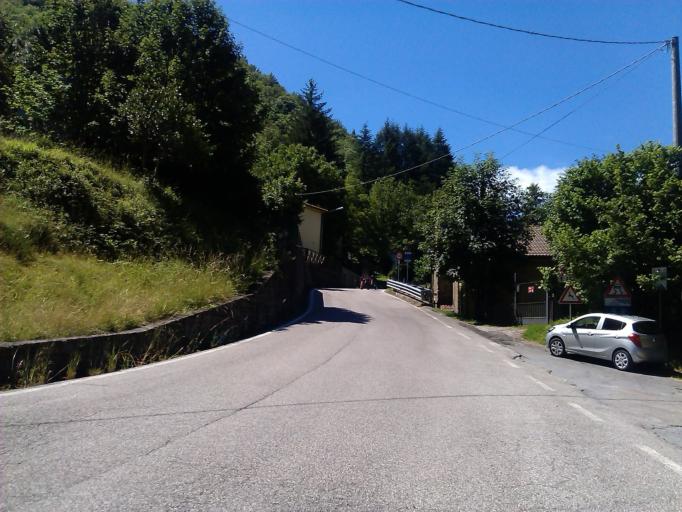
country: IT
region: Tuscany
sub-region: Provincia di Prato
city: Cantagallo
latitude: 44.0517
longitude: 11.0457
